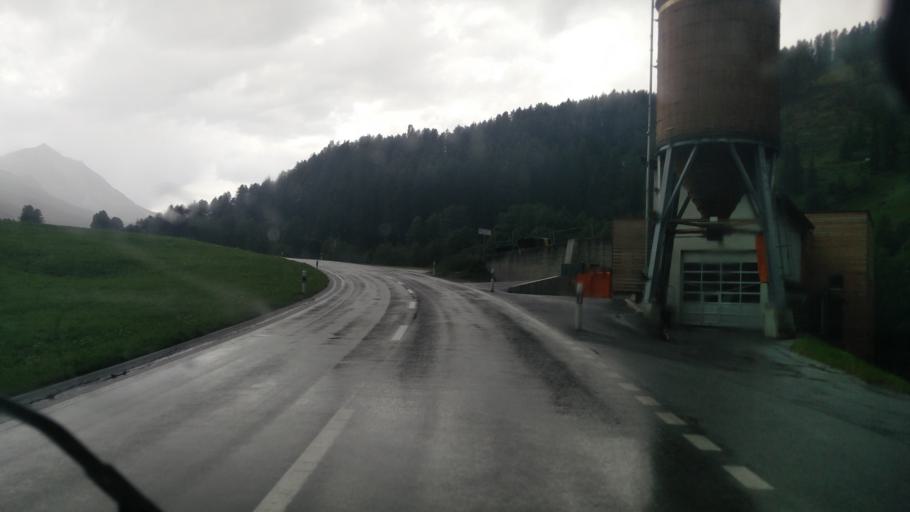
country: IT
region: Trentino-Alto Adige
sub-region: Bolzano
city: Tubre
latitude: 46.6057
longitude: 10.3903
